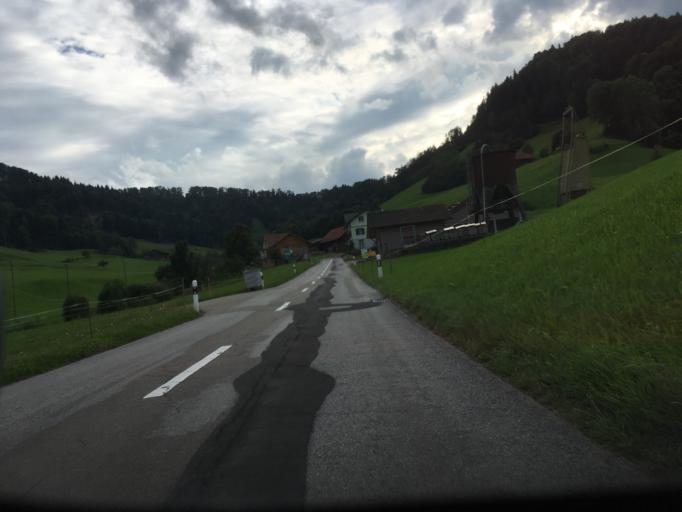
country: CH
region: Thurgau
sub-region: Muenchwilen District
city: Fischingen
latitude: 47.3696
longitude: 8.9825
